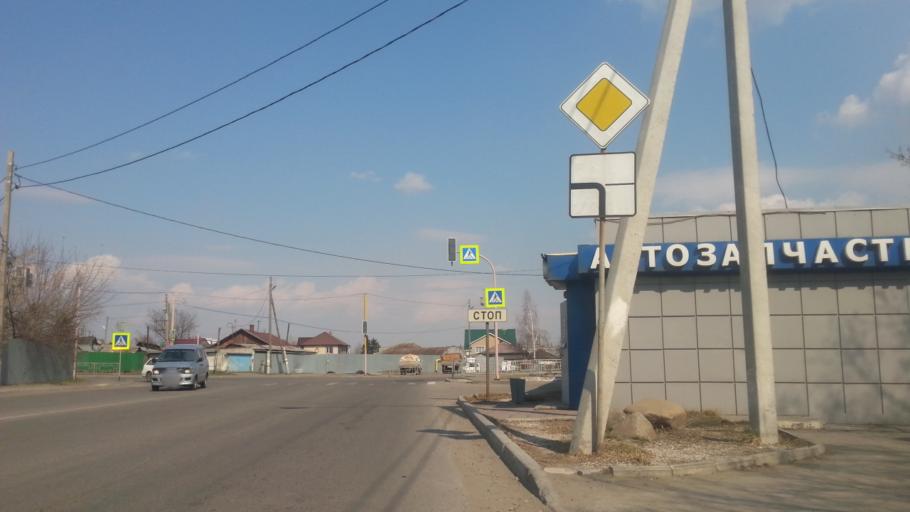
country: RU
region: Altai Krai
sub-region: Gorod Barnaulskiy
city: Barnaul
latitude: 53.3228
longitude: 83.7668
